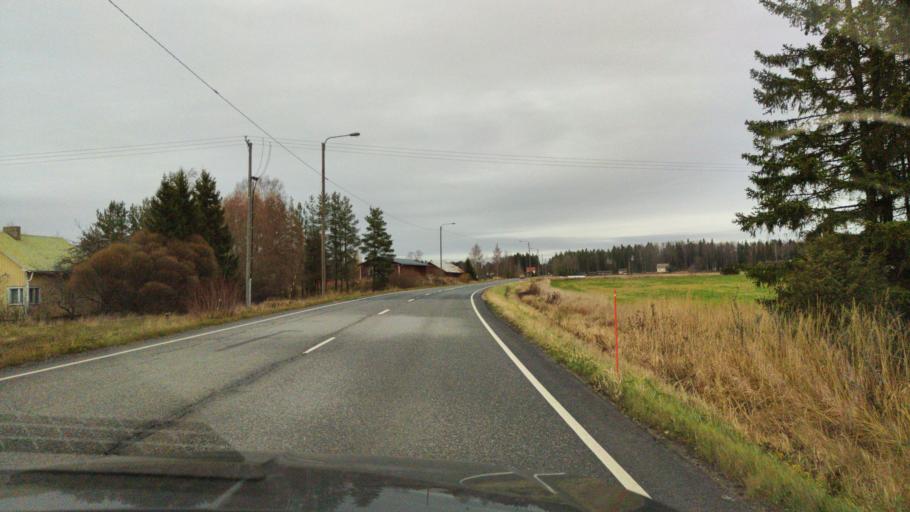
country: FI
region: Varsinais-Suomi
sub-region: Turku
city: Vahto
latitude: 60.6463
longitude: 22.4230
